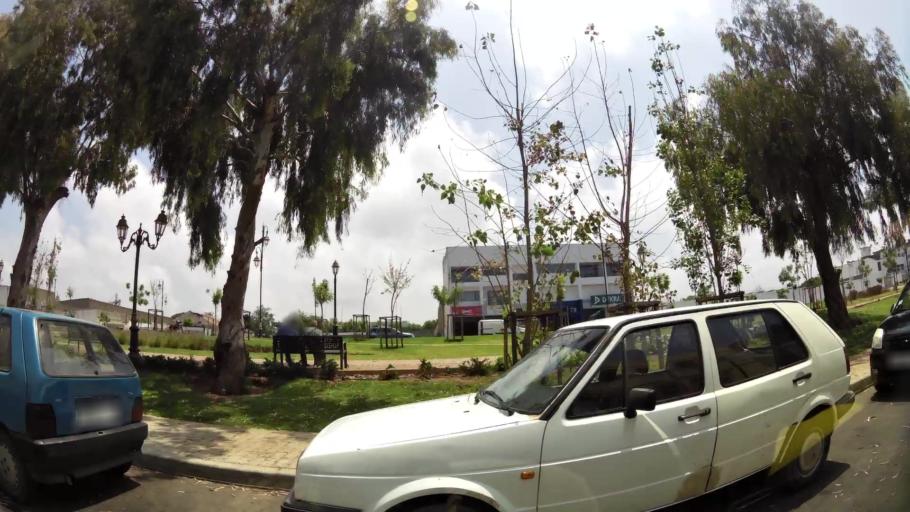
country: MA
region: Rabat-Sale-Zemmour-Zaer
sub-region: Rabat
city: Rabat
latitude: 33.9883
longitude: -6.8727
